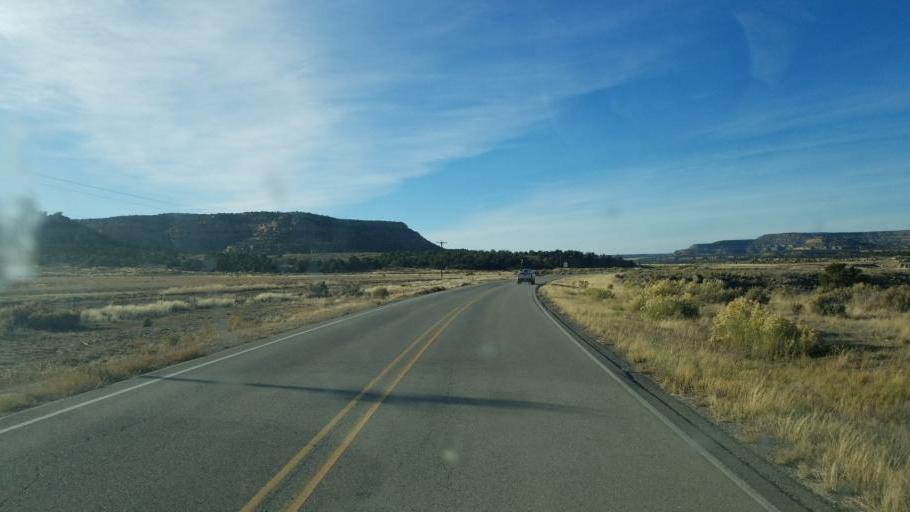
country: US
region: New Mexico
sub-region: San Juan County
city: Bloomfield
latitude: 36.7271
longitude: -107.5624
